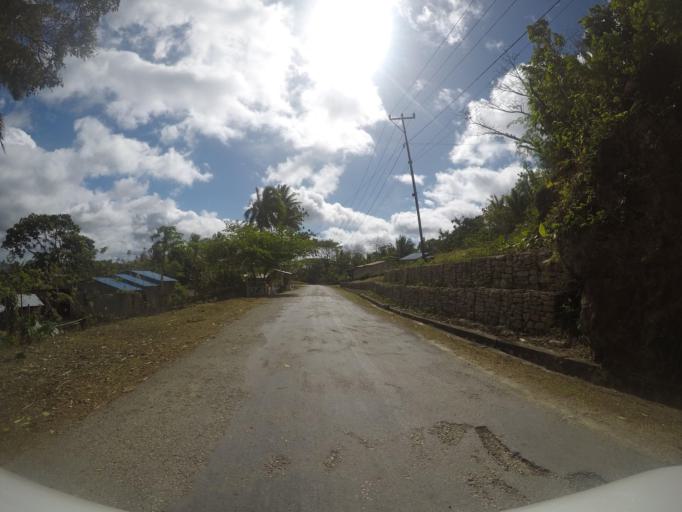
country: TL
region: Lautem
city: Lospalos
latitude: -8.5323
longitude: 126.9231
